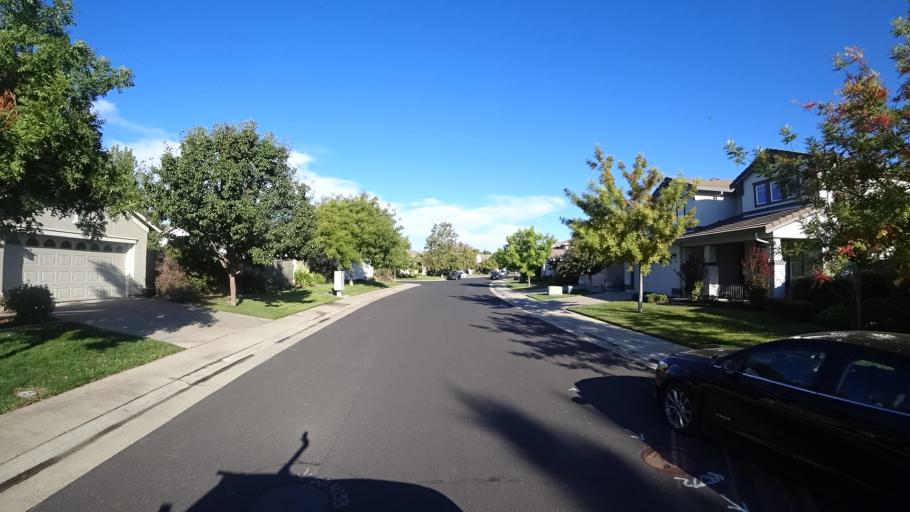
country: US
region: California
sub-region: Sacramento County
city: Laguna
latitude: 38.4022
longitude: -121.4672
